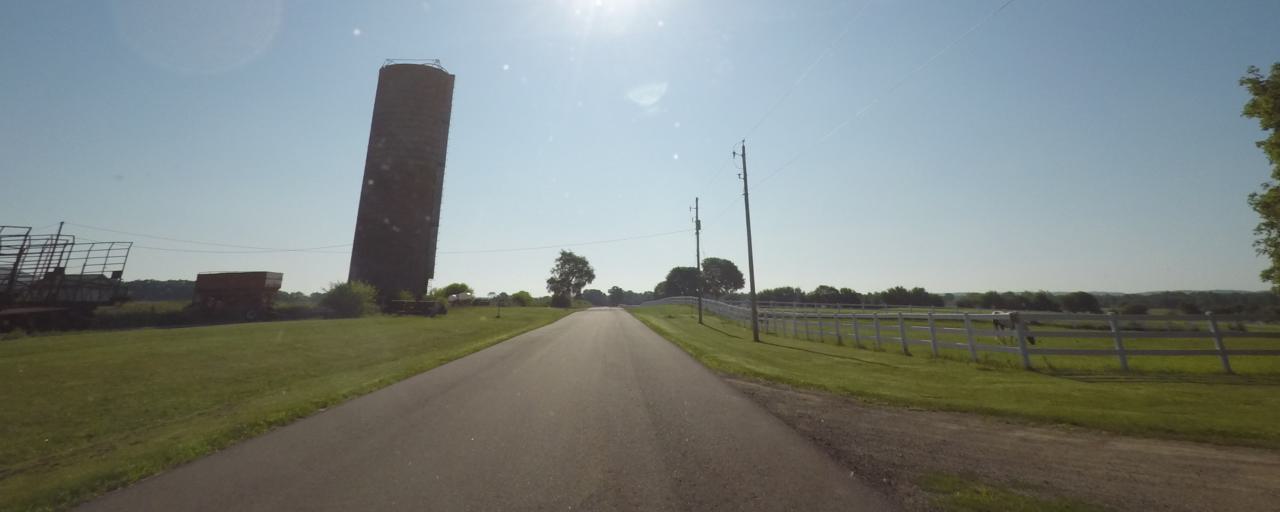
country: US
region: Wisconsin
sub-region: Jefferson County
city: Palmyra
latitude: 42.9189
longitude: -88.5554
